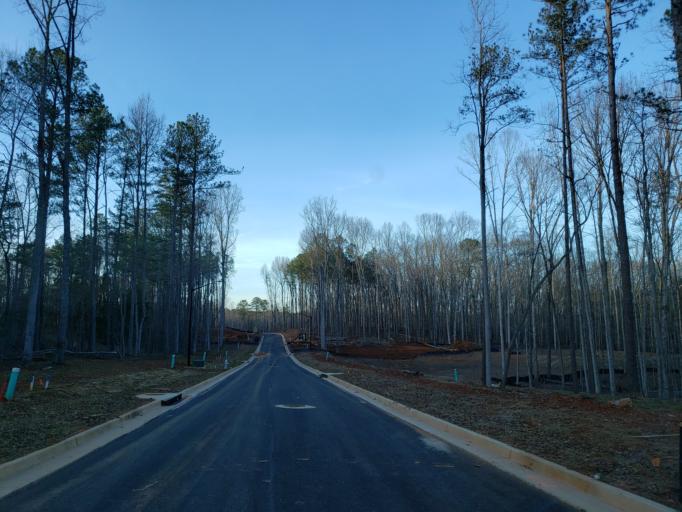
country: US
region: Georgia
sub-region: Cobb County
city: Acworth
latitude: 34.0274
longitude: -84.7310
